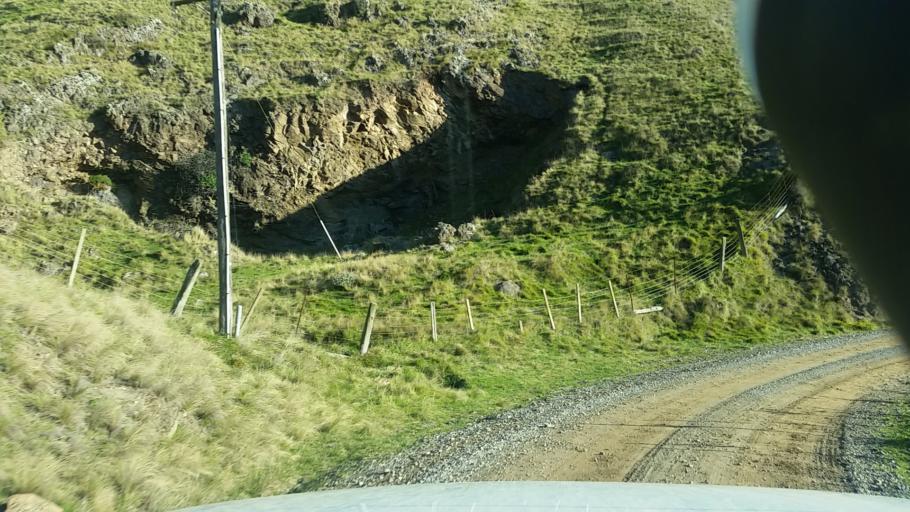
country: NZ
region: Canterbury
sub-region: Christchurch City
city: Christchurch
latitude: -43.6206
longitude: 172.7688
